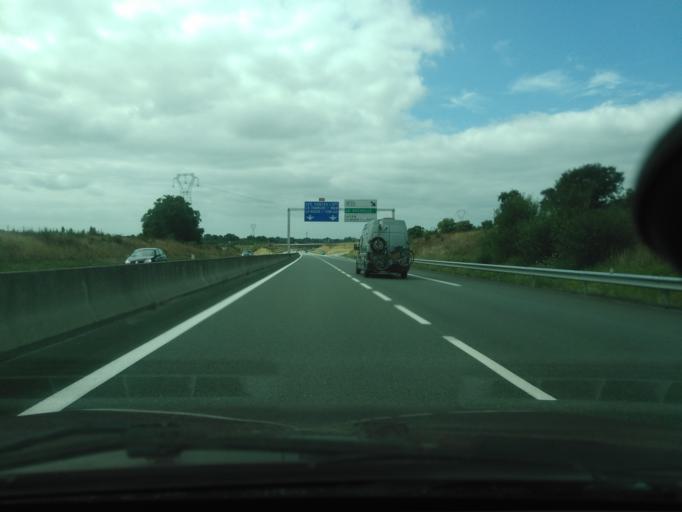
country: FR
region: Pays de la Loire
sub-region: Departement de la Vendee
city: La Roche-sur-Yon
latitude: 46.6421
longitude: -1.3951
